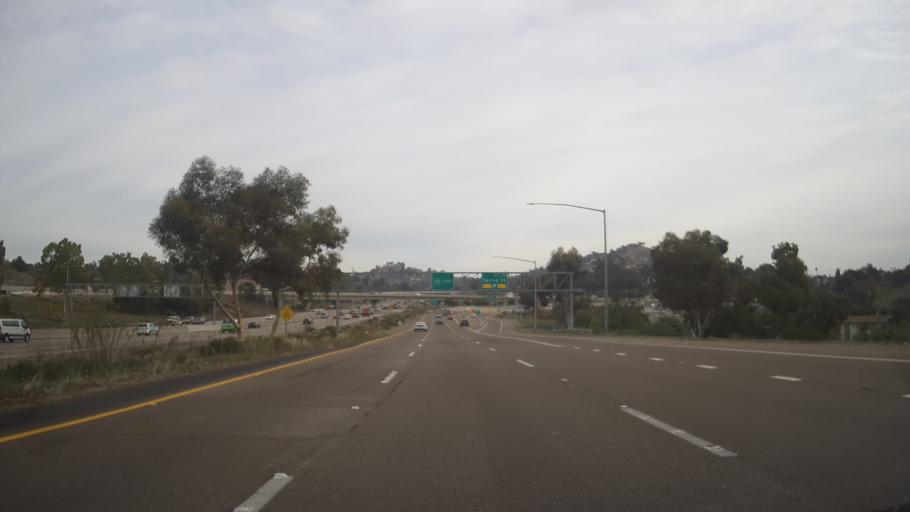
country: US
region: California
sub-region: San Diego County
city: Spring Valley
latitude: 32.7501
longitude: -117.0146
